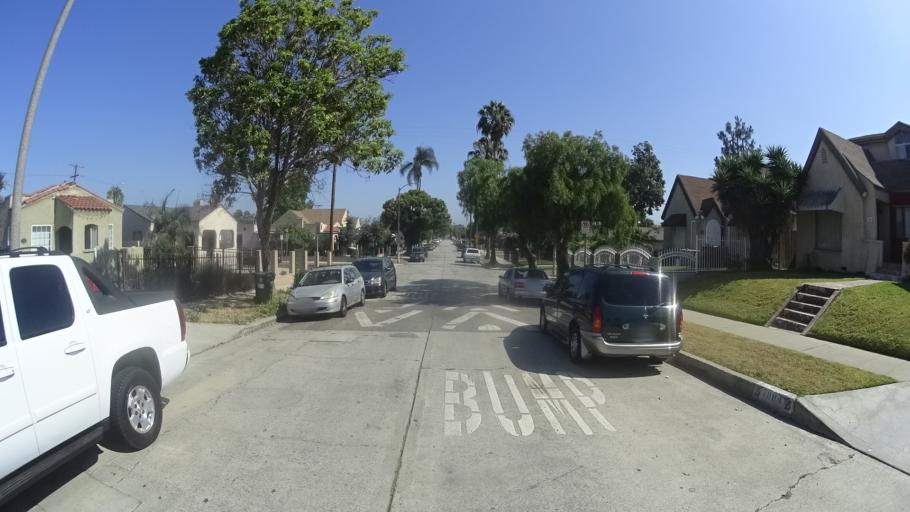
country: US
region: California
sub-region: Los Angeles County
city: View Park-Windsor Hills
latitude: 33.9760
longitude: -118.3226
